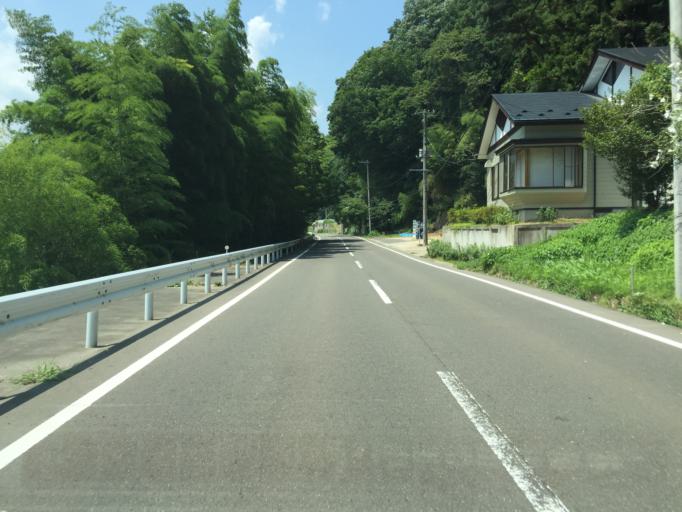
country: JP
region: Miyagi
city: Marumori
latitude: 37.9356
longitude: 140.7077
